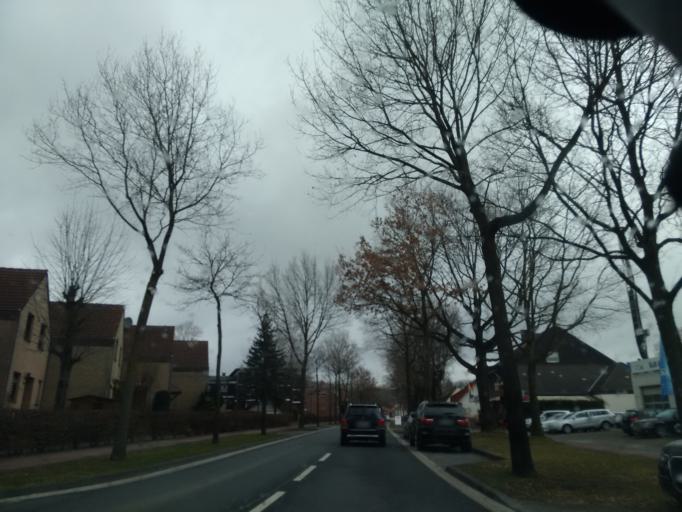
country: DE
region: North Rhine-Westphalia
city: Bad Lippspringe
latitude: 51.7627
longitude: 8.7853
